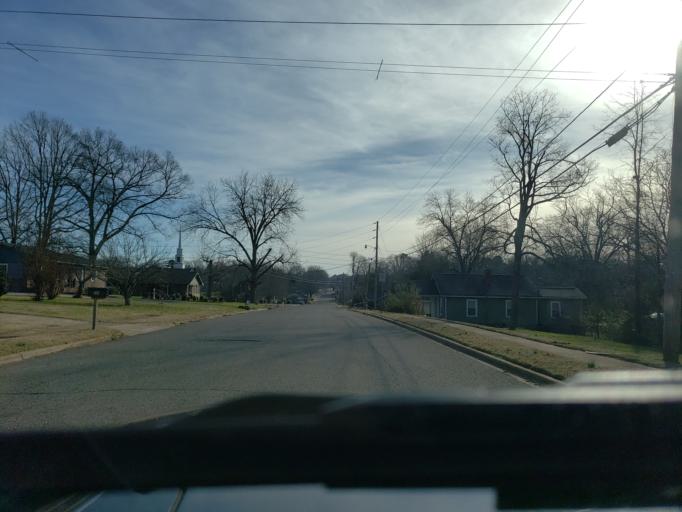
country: US
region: North Carolina
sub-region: Cleveland County
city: Kings Mountain
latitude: 35.2451
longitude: -81.3508
